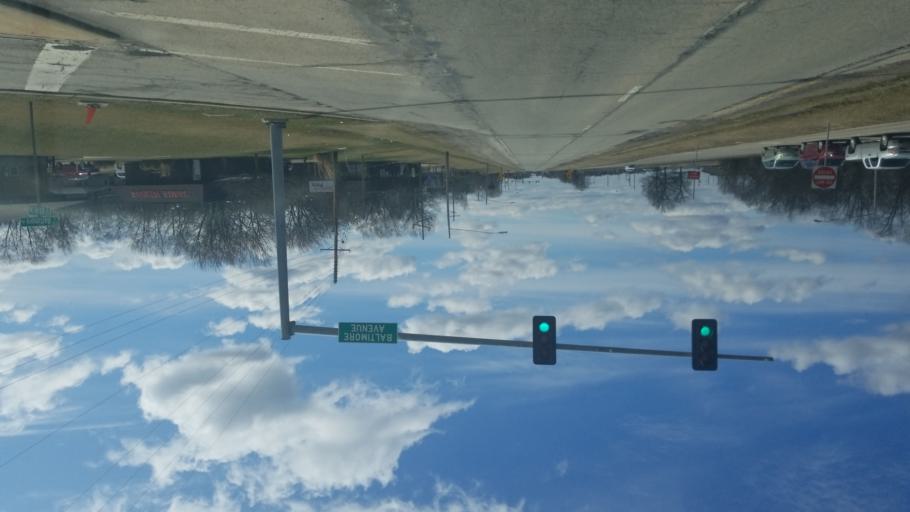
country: US
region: Illinois
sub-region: Macon County
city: Long Creek
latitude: 39.8243
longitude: -88.8925
